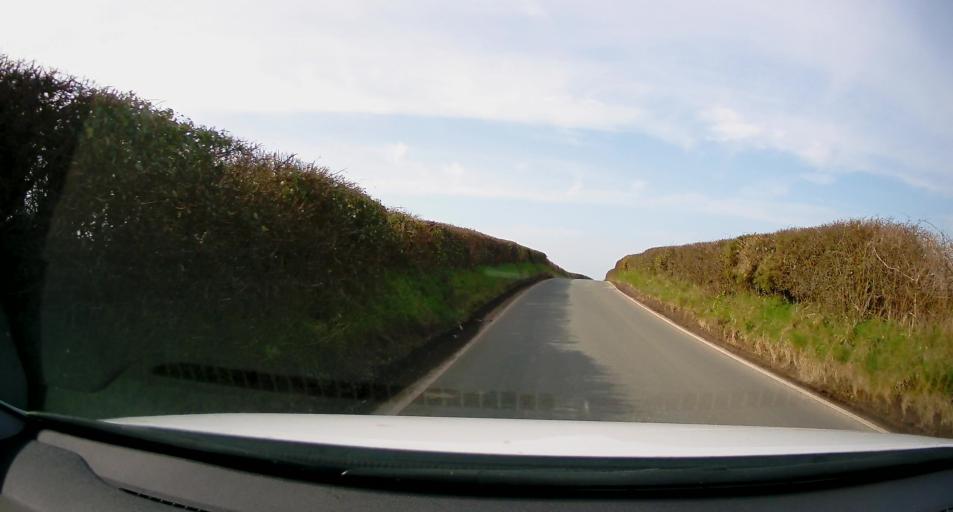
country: GB
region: Wales
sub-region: County of Ceredigion
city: Llanon
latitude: 52.2528
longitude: -4.2112
